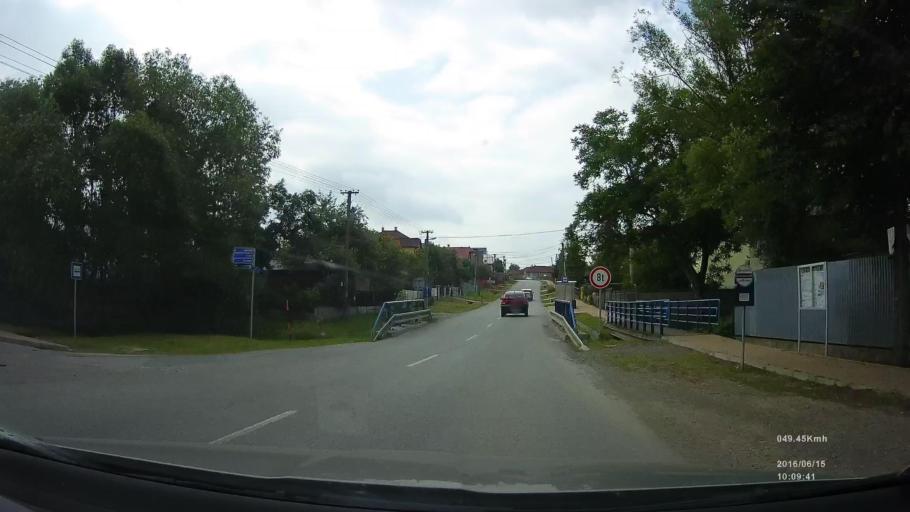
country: SK
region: Kosicky
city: Kosice
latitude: 48.7576
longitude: 21.3414
